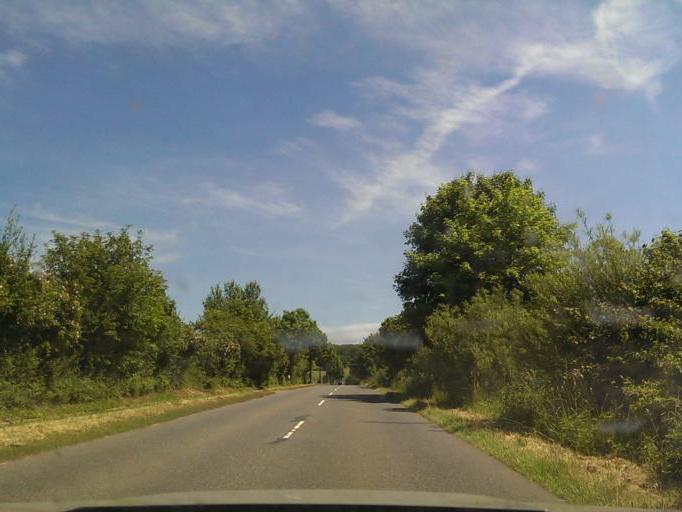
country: DE
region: Lower Saxony
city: Hoyershausen
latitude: 51.9863
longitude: 9.7748
